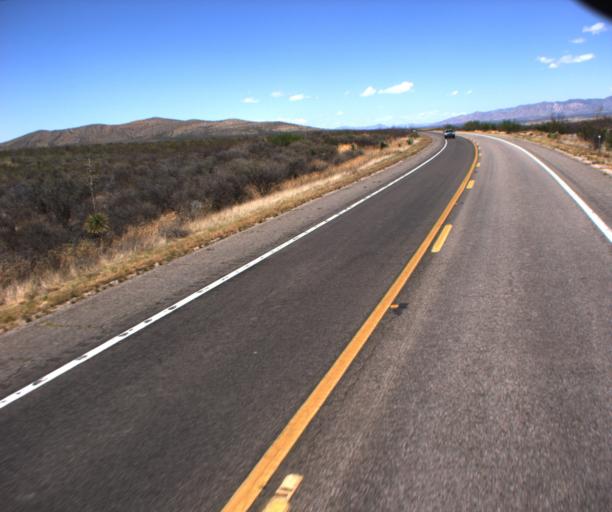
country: US
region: Arizona
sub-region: Cochise County
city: Tombstone
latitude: 31.6606
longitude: -110.0310
